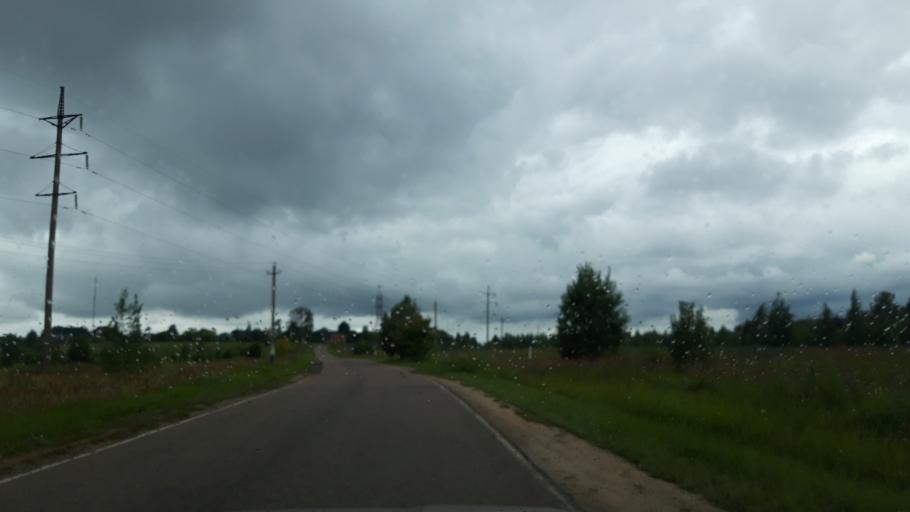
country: RU
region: Moskovskaya
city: Lozhki
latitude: 56.0896
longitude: 37.0776
